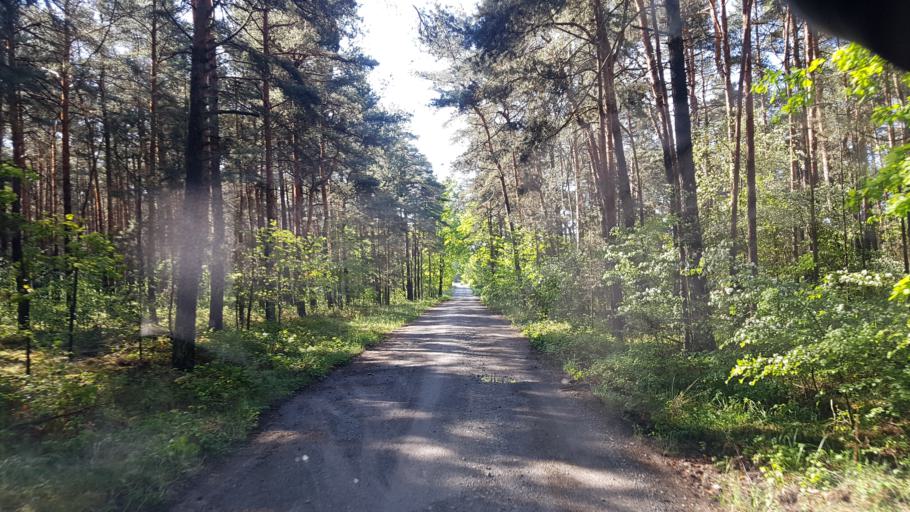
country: DE
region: Brandenburg
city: Grossraschen
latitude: 51.5923
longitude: 13.9602
